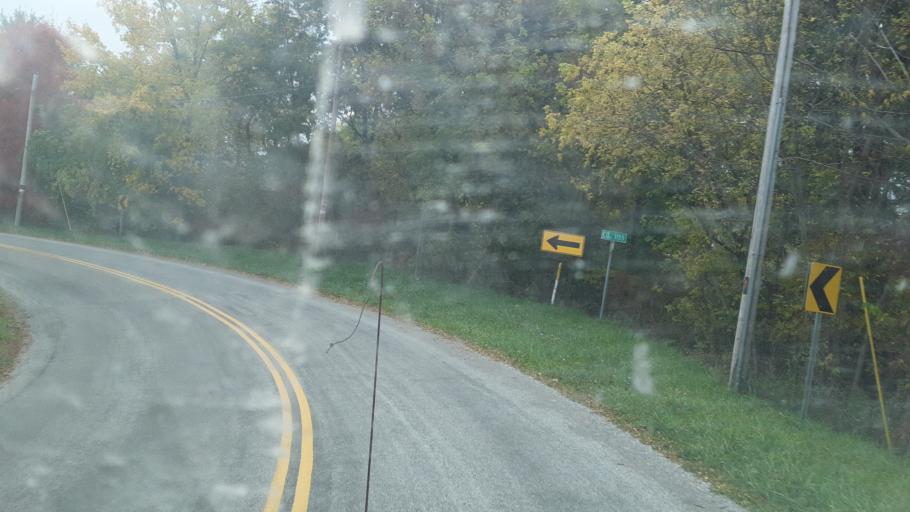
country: US
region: Ohio
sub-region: Ashland County
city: Ashland
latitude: 40.7853
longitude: -82.3490
